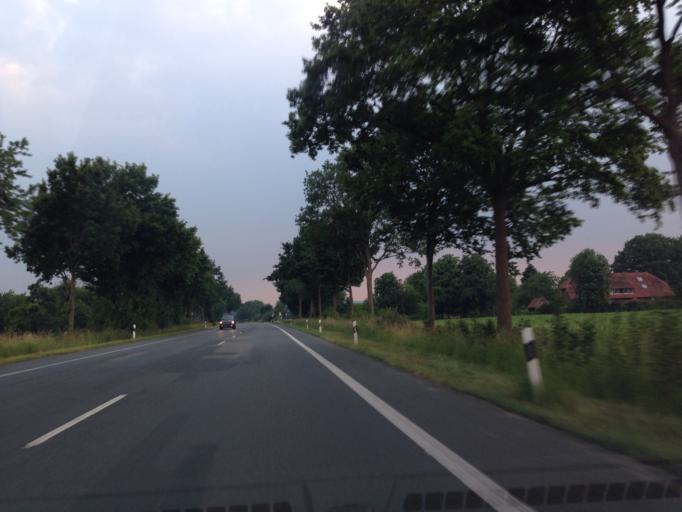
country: DE
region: North Rhine-Westphalia
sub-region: Regierungsbezirk Munster
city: Altenberge
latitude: 51.9839
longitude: 7.5338
